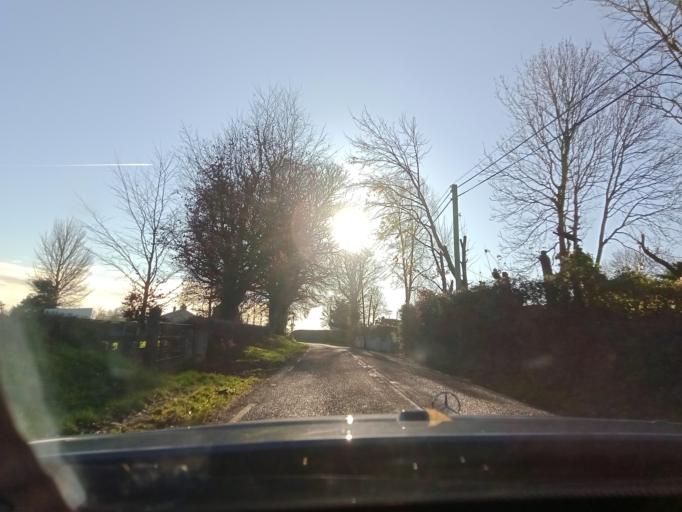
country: IE
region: Leinster
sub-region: Kilkenny
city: Piltown
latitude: 52.3751
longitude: -7.3398
